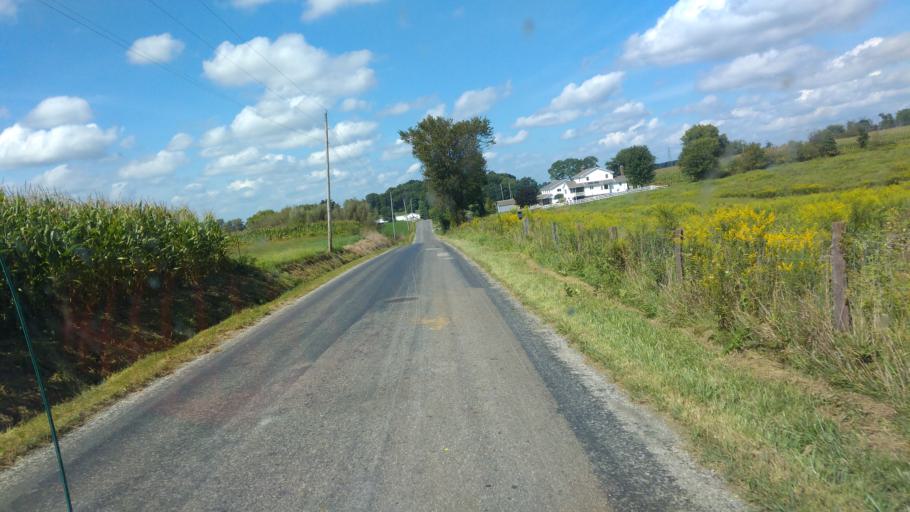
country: US
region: Ohio
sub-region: Wayne County
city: Apple Creek
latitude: 40.6426
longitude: -81.8516
